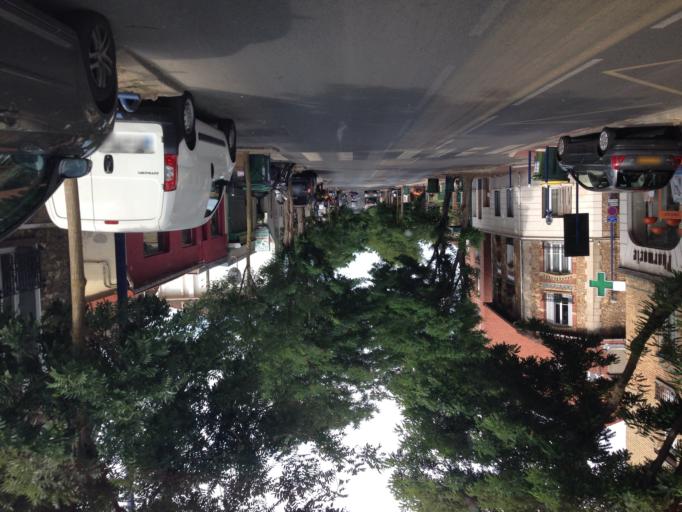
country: FR
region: Ile-de-France
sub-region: Departement des Hauts-de-Seine
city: Clamart
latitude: 48.8070
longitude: 2.2538
